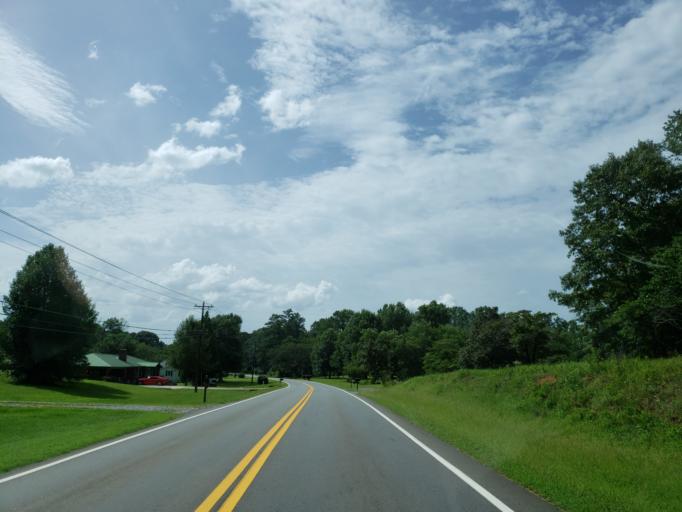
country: US
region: Georgia
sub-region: Cherokee County
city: Canton
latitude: 34.3013
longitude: -84.4509
